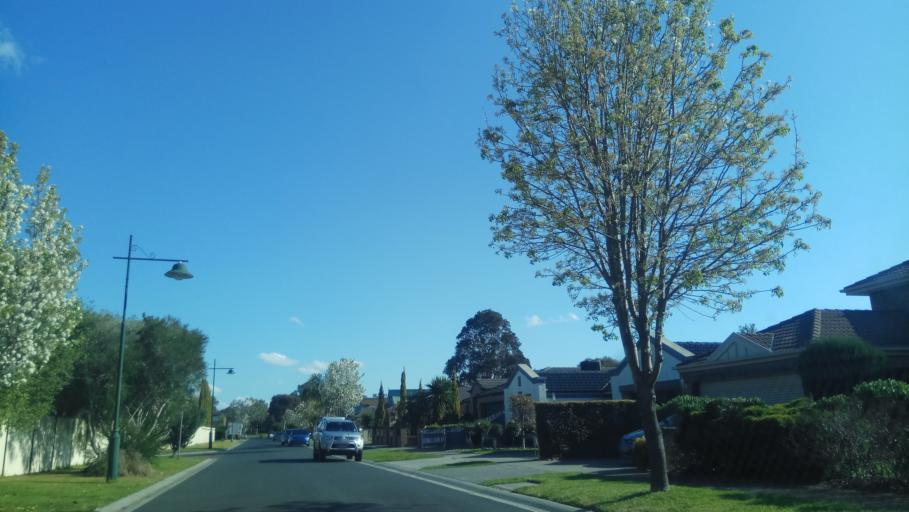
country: AU
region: Victoria
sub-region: Kingston
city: Dingley Village
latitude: -37.9864
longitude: 145.1274
